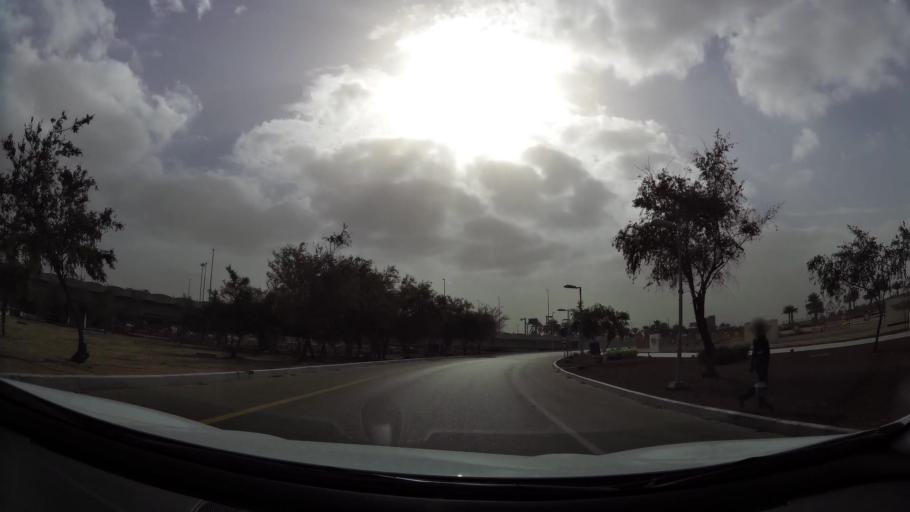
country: AE
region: Abu Dhabi
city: Abu Dhabi
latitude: 24.4178
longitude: 54.4768
